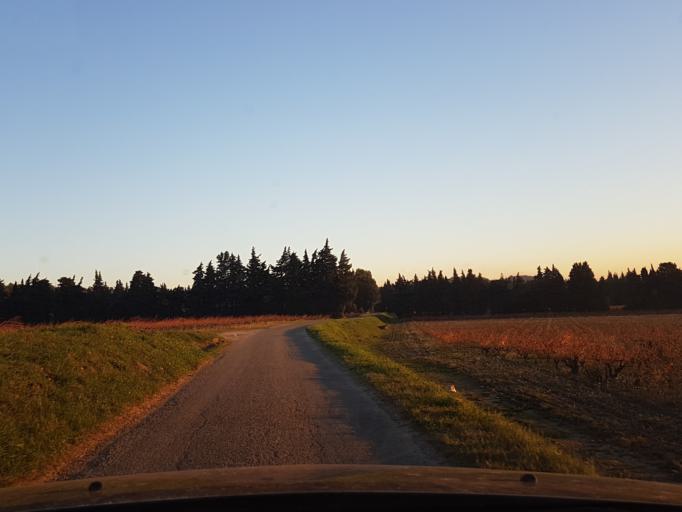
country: FR
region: Provence-Alpes-Cote d'Azur
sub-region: Departement du Vaucluse
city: Saint-Saturnin-les-Avignon
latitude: 43.9600
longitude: 4.9136
